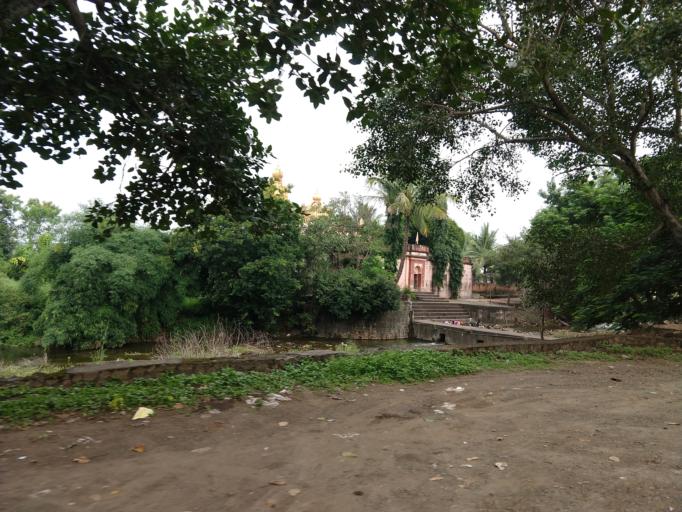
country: IN
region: Maharashtra
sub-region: Pune Division
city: Sasvad
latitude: 18.3593
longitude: 73.9960
